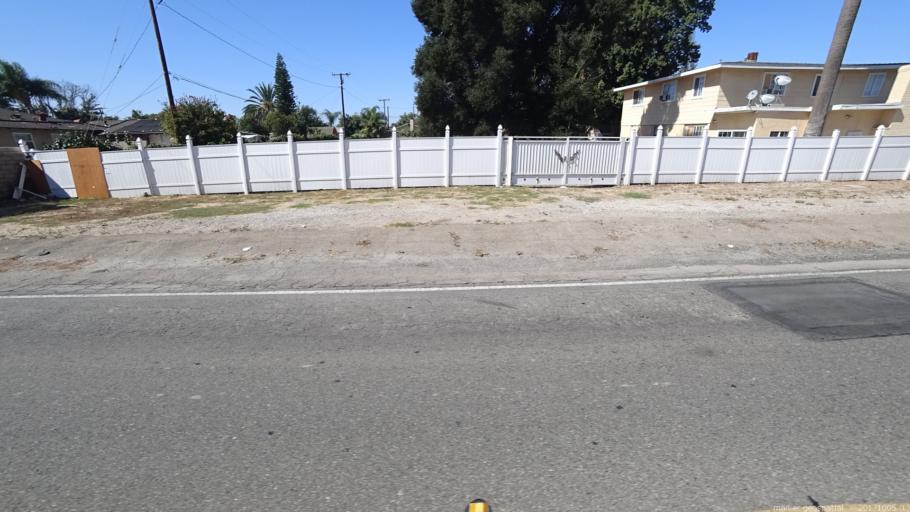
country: US
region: California
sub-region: Orange County
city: Garden Grove
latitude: 33.7787
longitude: -117.9673
